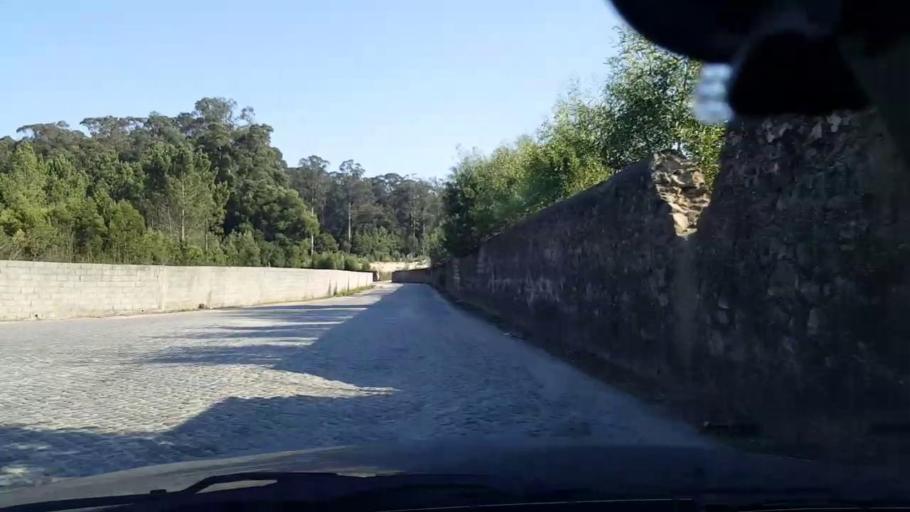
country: PT
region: Porto
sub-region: Vila do Conde
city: Arvore
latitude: 41.3476
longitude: -8.6922
